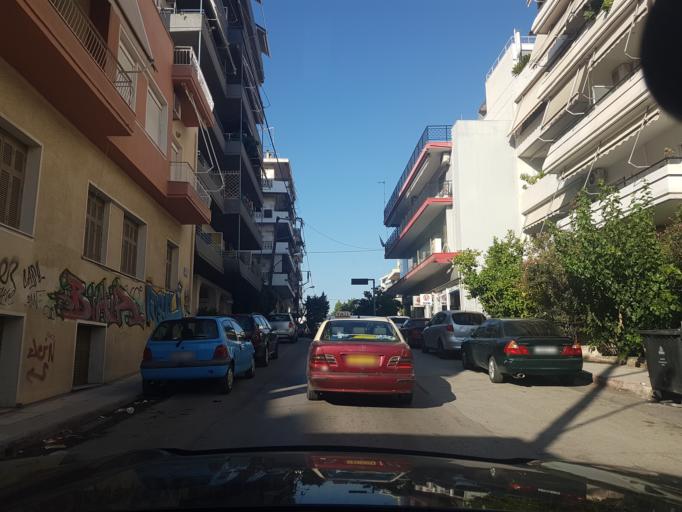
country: GR
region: Central Greece
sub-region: Nomos Evvoias
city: Chalkida
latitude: 38.4695
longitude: 23.5984
